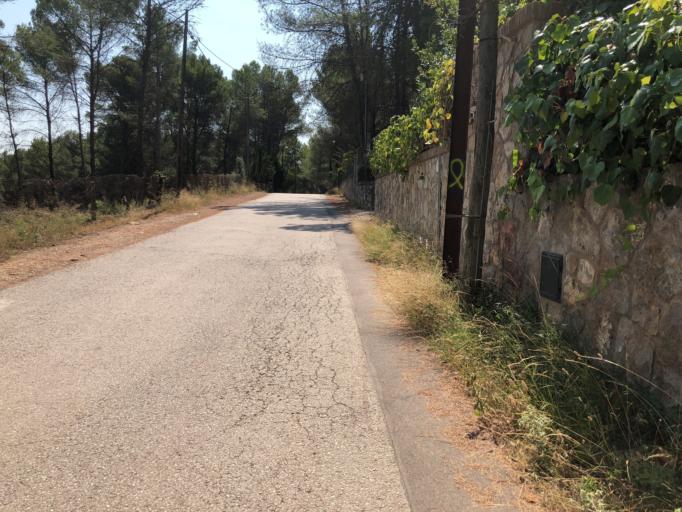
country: ES
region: Catalonia
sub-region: Provincia de Barcelona
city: Corbera de Llobregat
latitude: 41.4176
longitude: 1.9072
